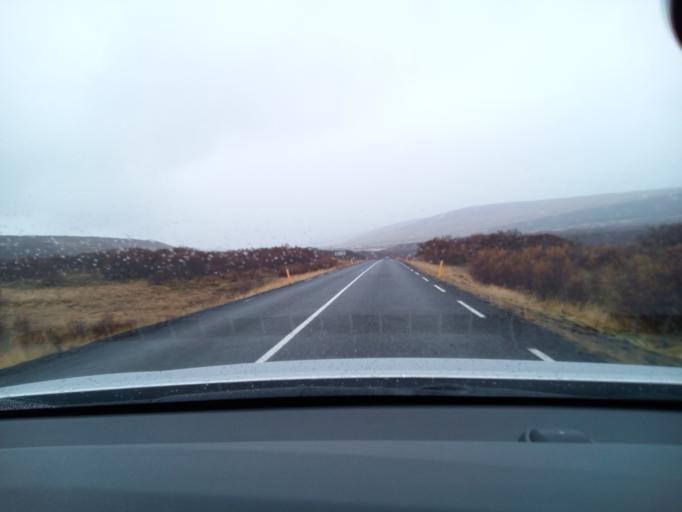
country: IS
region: South
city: Hveragerdi
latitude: 64.7013
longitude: -20.9831
